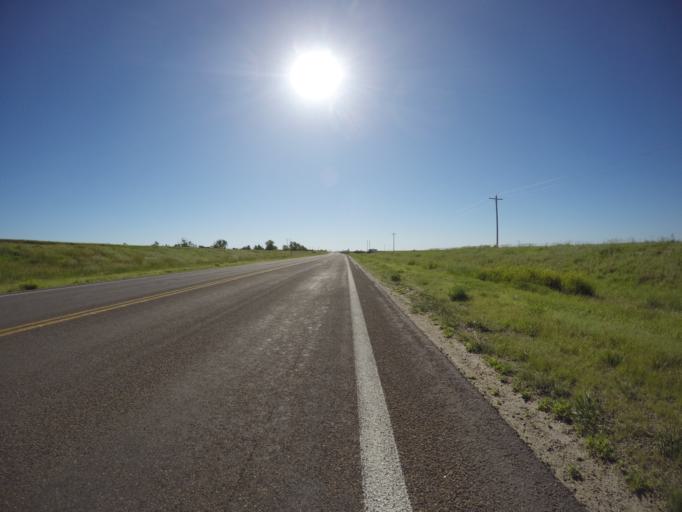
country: US
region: Kansas
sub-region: Norton County
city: Norton
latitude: 39.8277
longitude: -100.0076
